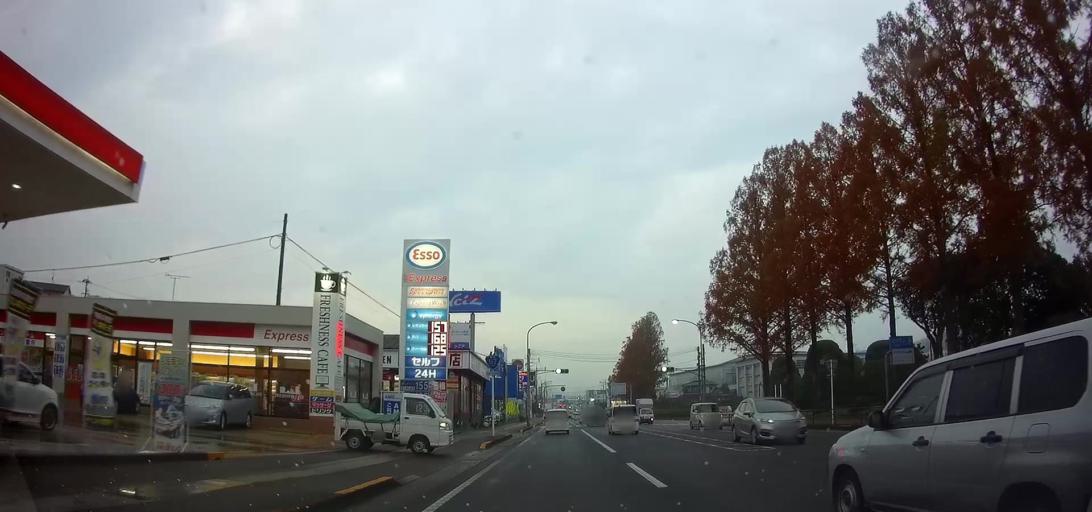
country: JP
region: Nagasaki
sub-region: Isahaya-shi
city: Isahaya
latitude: 32.8377
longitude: 130.0372
